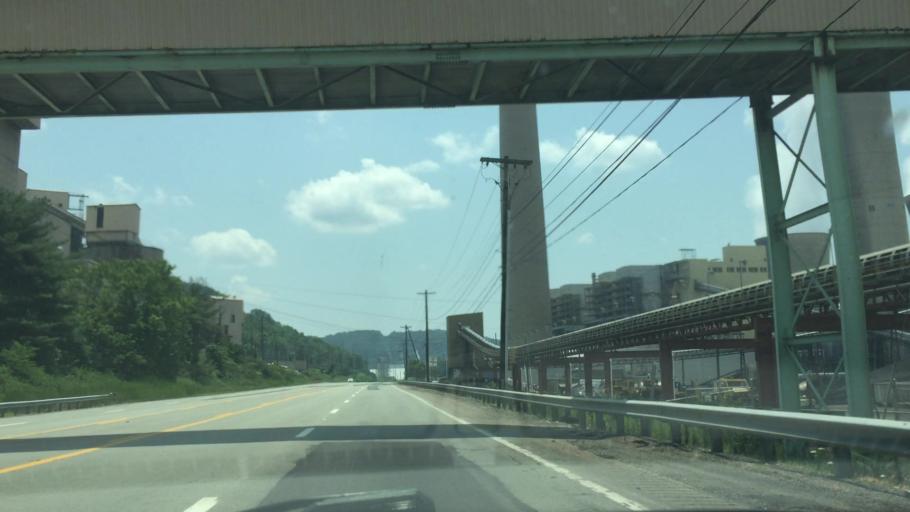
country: US
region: Ohio
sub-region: Belmont County
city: Powhatan Point
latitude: 39.8344
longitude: -80.8152
